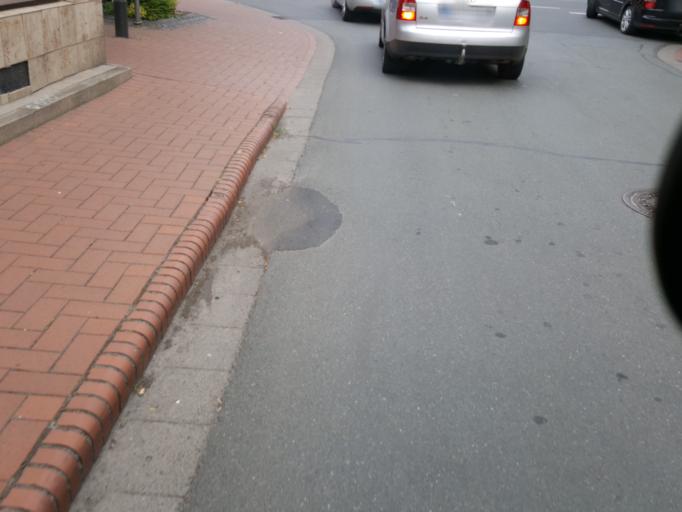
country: DE
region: Lower Saxony
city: Stolzenau
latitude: 52.5117
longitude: 9.0767
